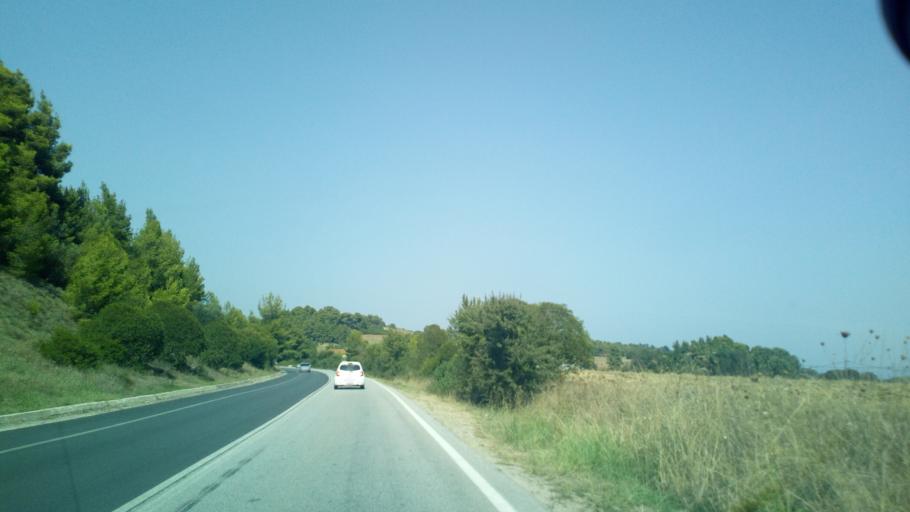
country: GR
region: Central Macedonia
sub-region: Nomos Chalkidikis
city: Kallithea
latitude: 40.0619
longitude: 23.4369
